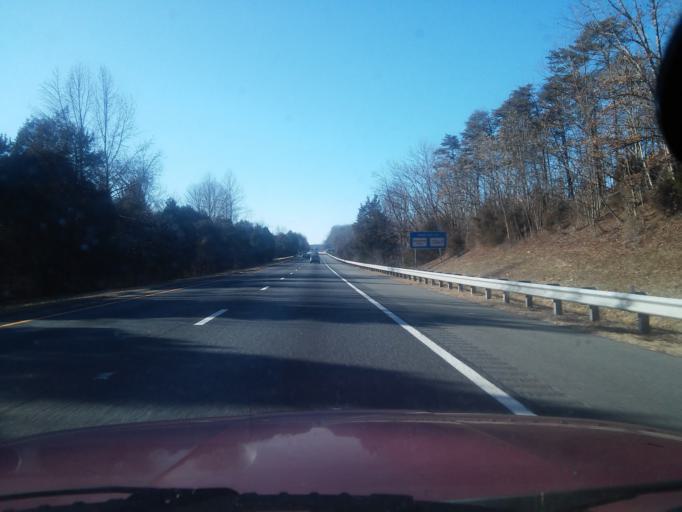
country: US
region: Virginia
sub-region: City of Charlottesville
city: Charlottesville
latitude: 38.0138
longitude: -78.3866
